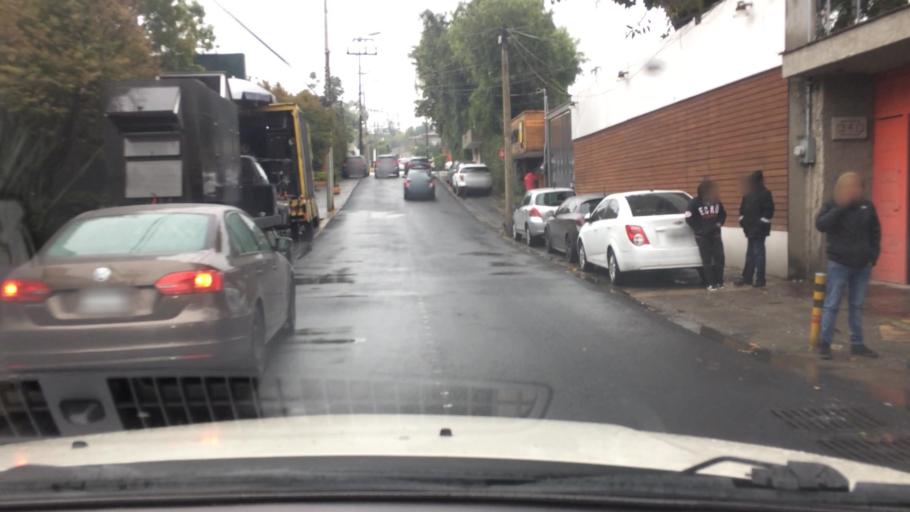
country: MX
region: Mexico City
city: Magdalena Contreras
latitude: 19.3231
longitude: -99.2058
